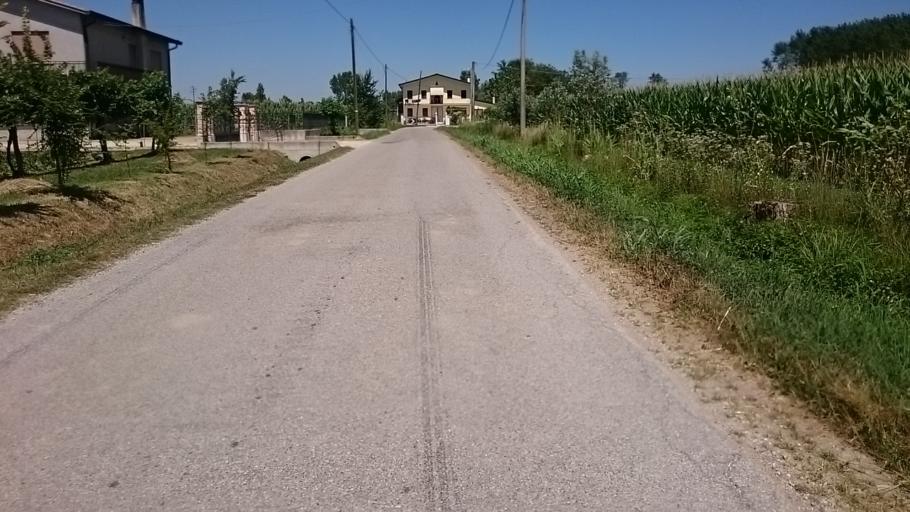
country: IT
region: Veneto
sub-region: Provincia di Padova
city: Borgoricco-San Michele delle Badesse-Sant'Eufemia
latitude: 45.5290
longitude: 11.9235
